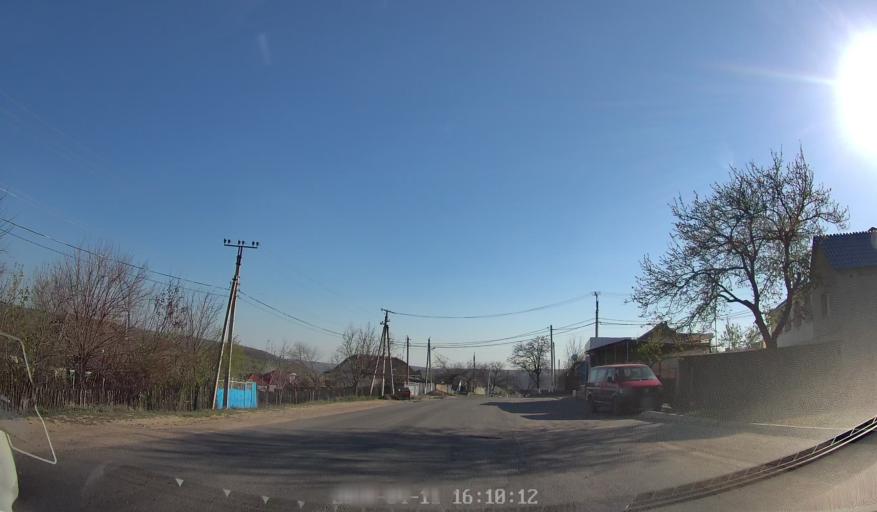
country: MD
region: Chisinau
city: Vadul lui Voda
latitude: 47.0691
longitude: 29.1346
